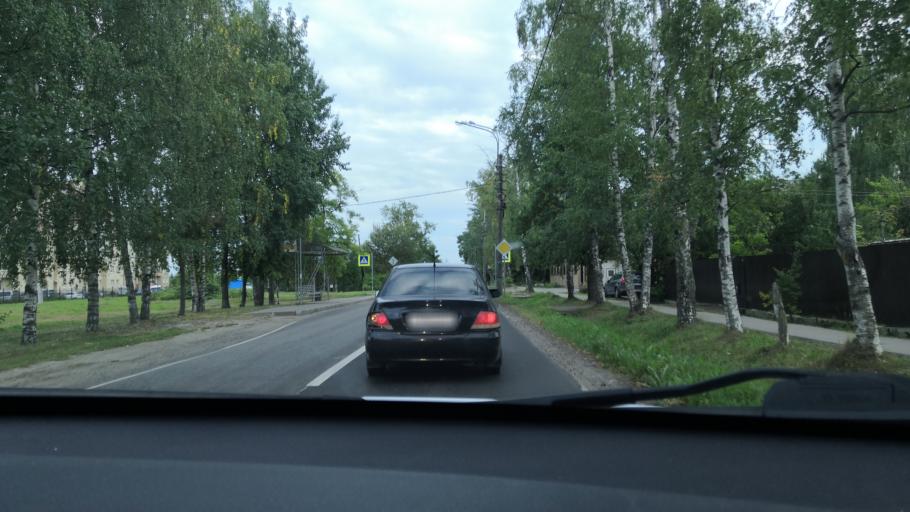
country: RU
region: St.-Petersburg
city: Pushkin
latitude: 59.6972
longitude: 30.4114
